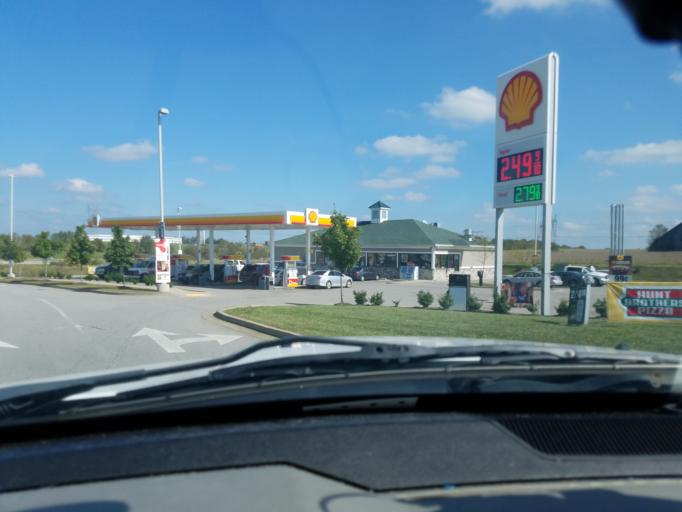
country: US
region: Kentucky
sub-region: Woodford County
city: Midway
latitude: 38.1574
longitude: -84.6762
